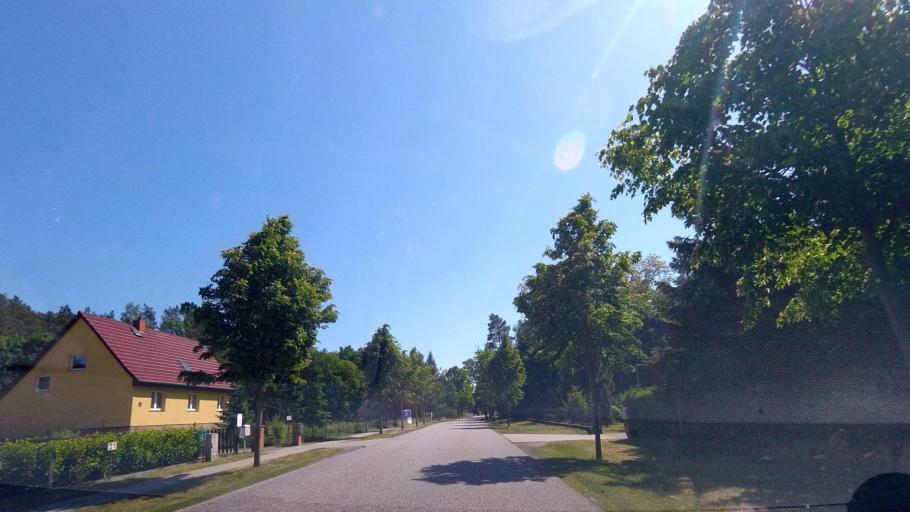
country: DE
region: Brandenburg
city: Gross Kreutz
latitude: 52.3583
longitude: 12.7657
